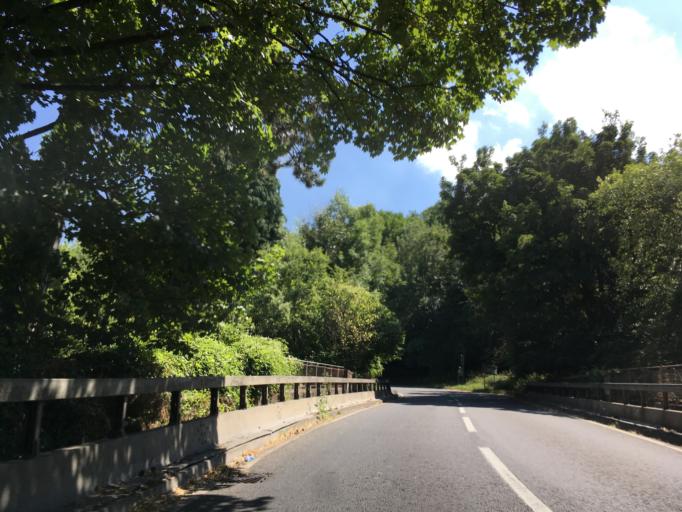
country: GB
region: England
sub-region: Gloucestershire
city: Chalford
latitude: 51.7209
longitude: -2.1498
